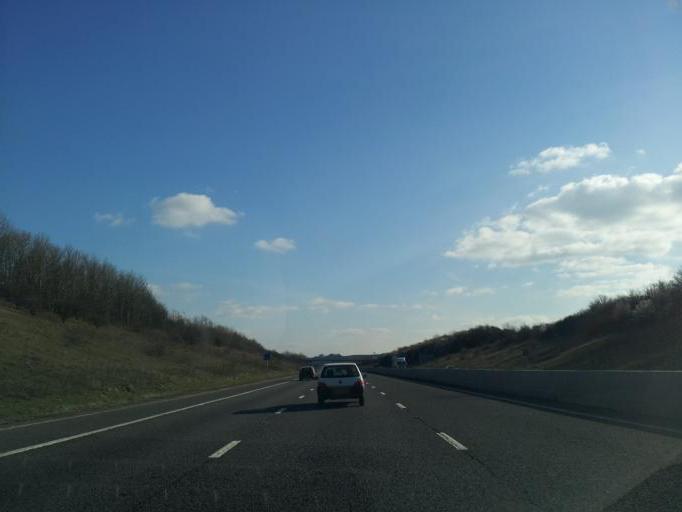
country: GB
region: England
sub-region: North Somerset
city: St. Georges
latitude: 51.3446
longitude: -2.8948
